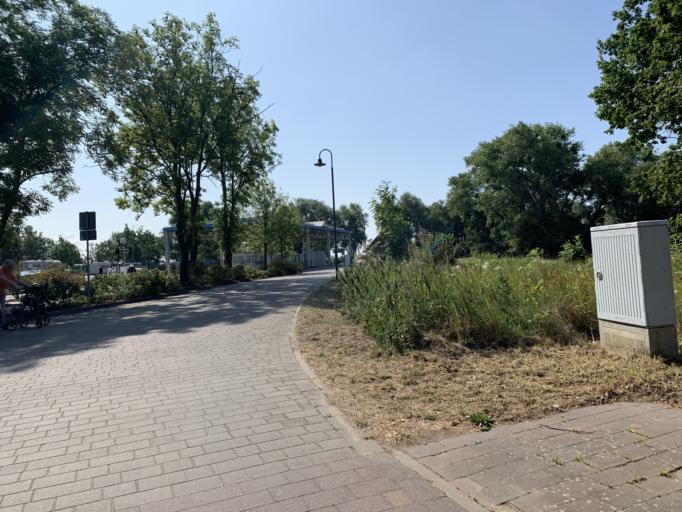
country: PL
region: West Pomeranian Voivodeship
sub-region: Powiat policki
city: Nowe Warpno
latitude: 53.7390
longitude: 14.2697
